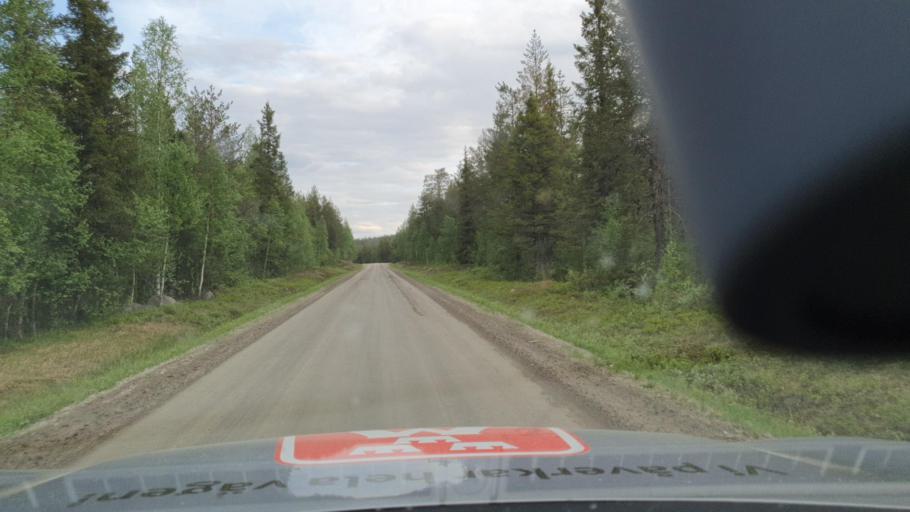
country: SE
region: Norrbotten
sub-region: Gallivare Kommun
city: Gaellivare
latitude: 66.7363
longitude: 21.1410
